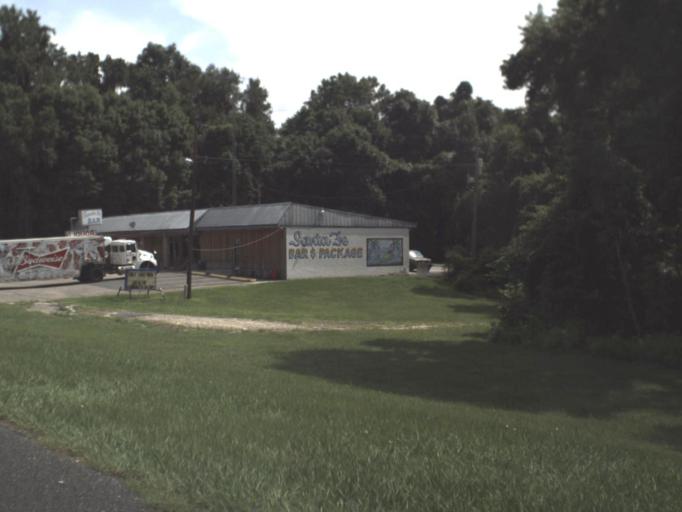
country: US
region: Florida
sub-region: Alachua County
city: High Springs
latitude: 29.8573
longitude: -82.6085
